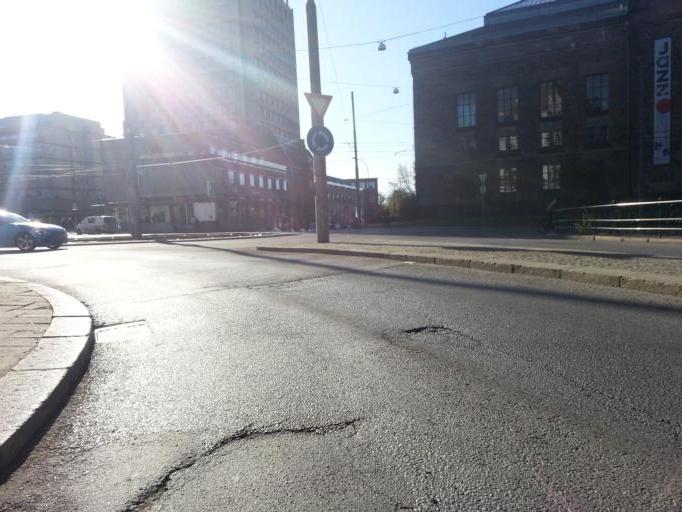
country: NO
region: Oslo
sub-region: Oslo
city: Oslo
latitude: 59.9148
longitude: 10.7172
